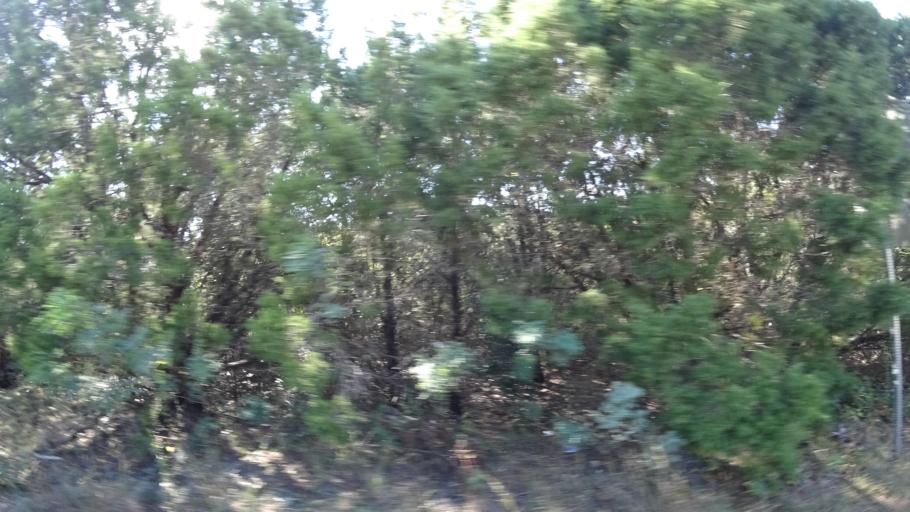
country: US
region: Texas
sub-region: Travis County
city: Barton Creek
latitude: 30.2324
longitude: -97.8713
